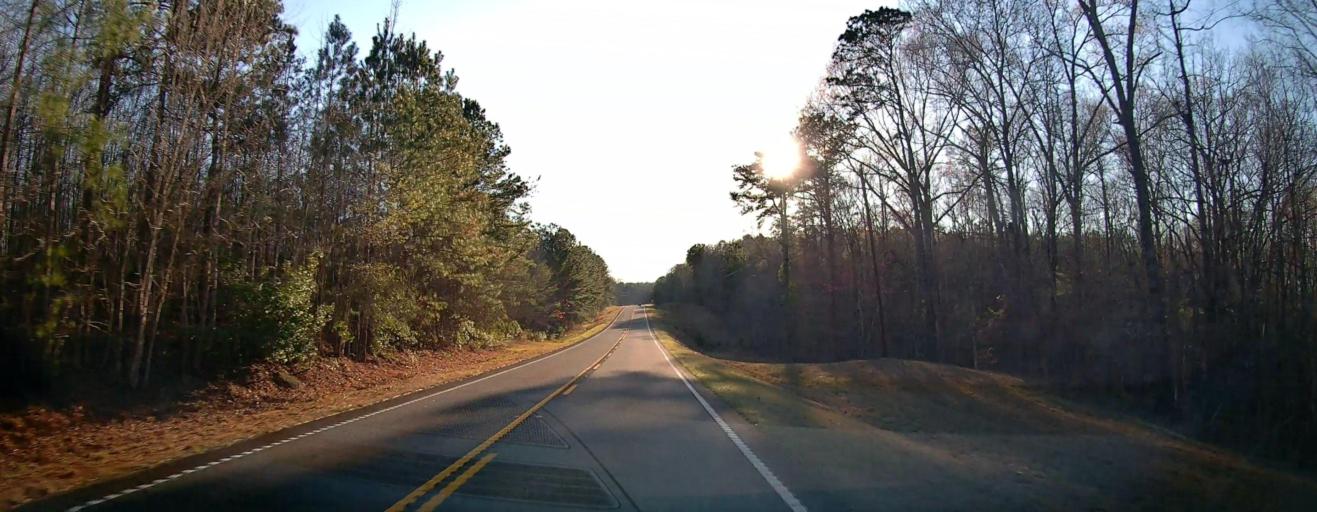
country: US
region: Georgia
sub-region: Talbot County
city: Talbotton
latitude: 32.6602
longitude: -84.6390
